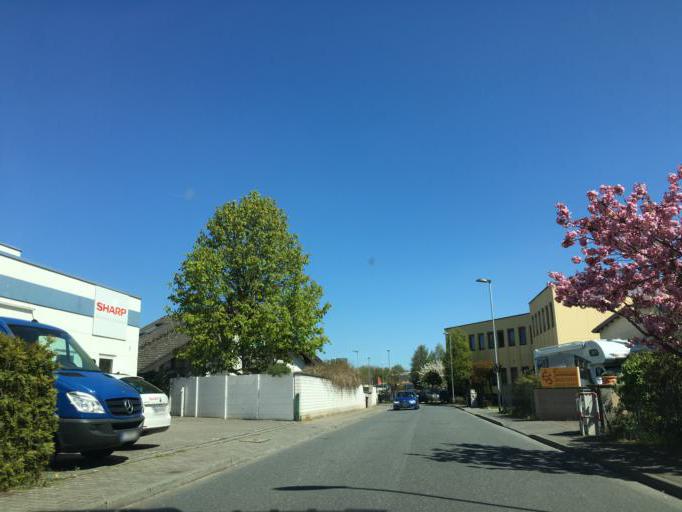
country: DE
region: Hesse
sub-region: Regierungsbezirk Darmstadt
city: Neu Isenburg
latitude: 50.0471
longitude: 8.7159
